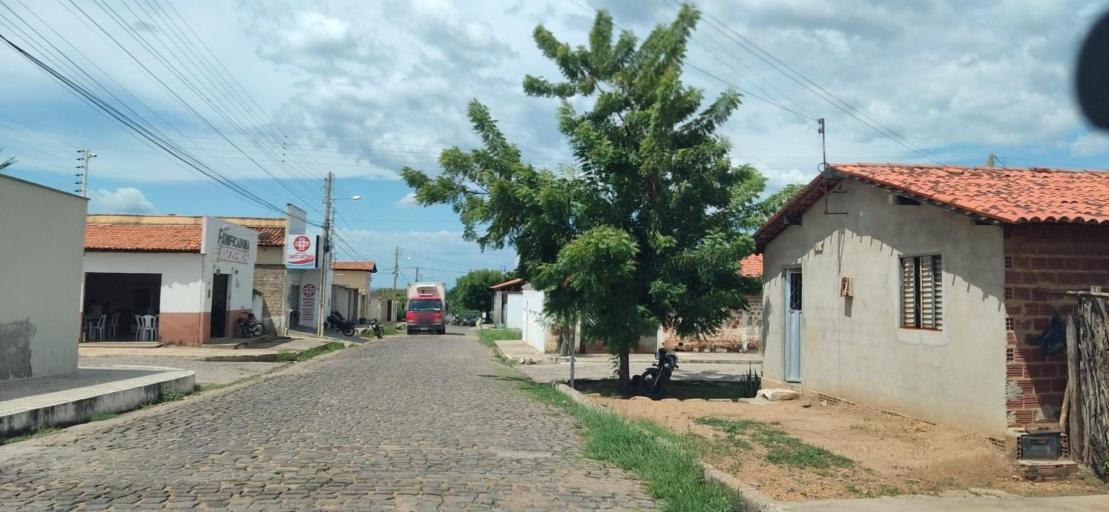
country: BR
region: Piaui
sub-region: Valenca Do Piaui
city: Valenca do Piaui
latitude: -6.4069
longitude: -41.7437
